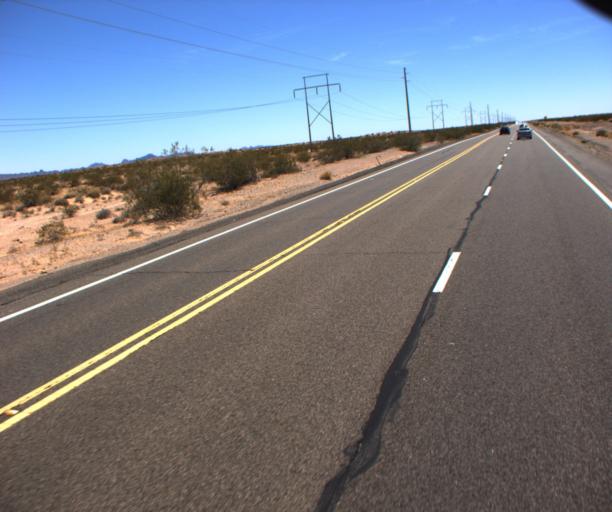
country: US
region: Arizona
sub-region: La Paz County
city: Parker
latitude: 33.9787
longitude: -114.2169
